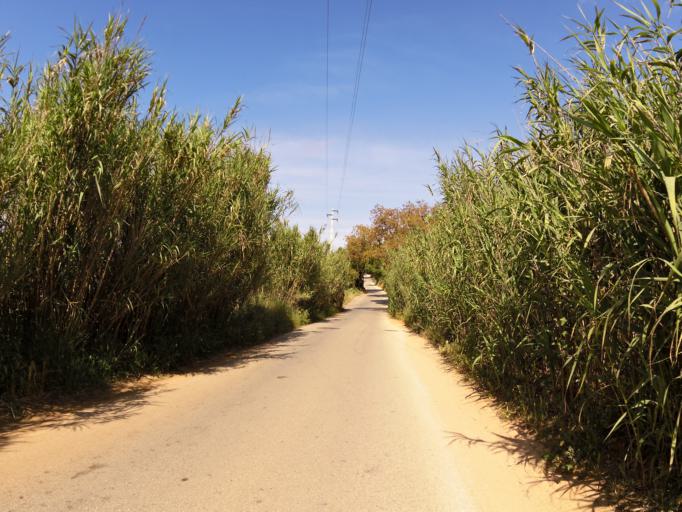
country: PT
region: Faro
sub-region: Loule
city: Almancil
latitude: 37.0675
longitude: -8.0073
